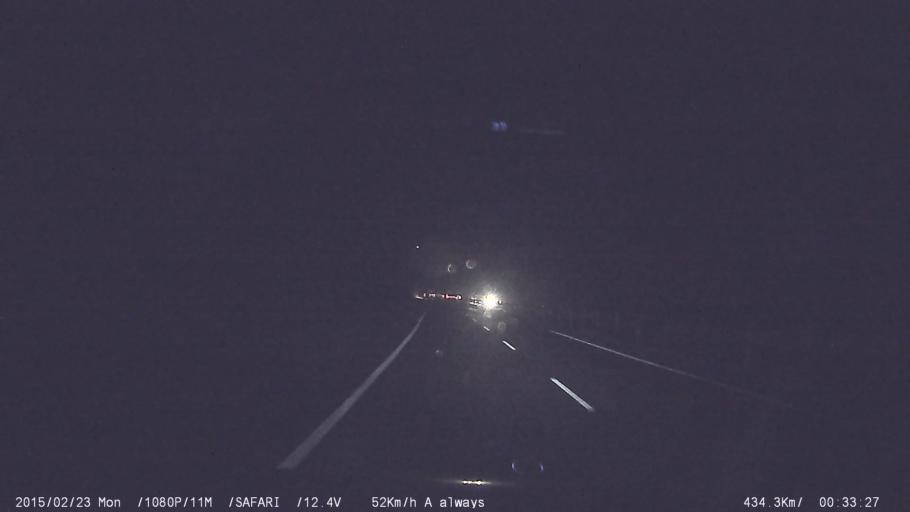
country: IN
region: Tamil Nadu
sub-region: Dharmapuri
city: Dharmapuri
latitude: 11.9737
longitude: 78.0528
